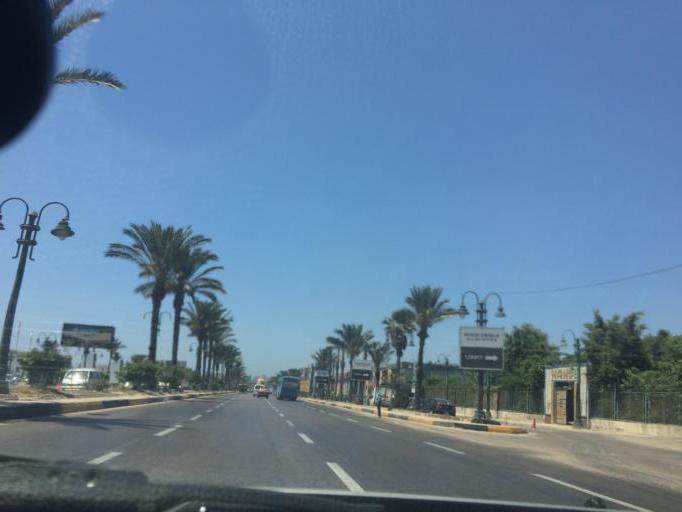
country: EG
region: Alexandria
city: Alexandria
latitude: 31.1715
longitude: 29.9336
